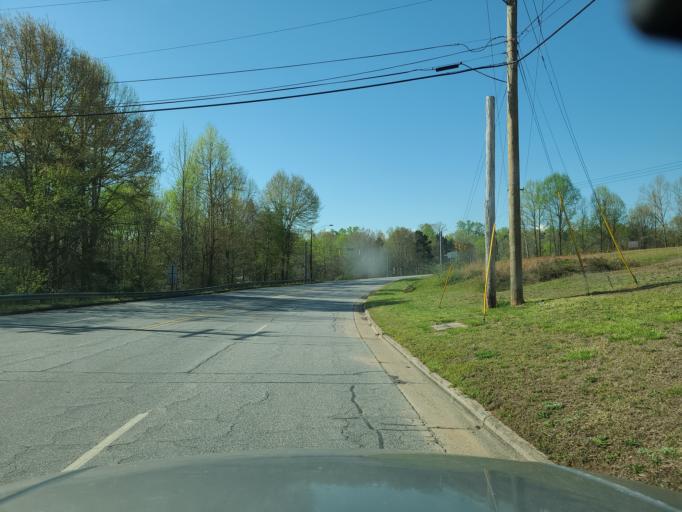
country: US
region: North Carolina
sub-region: Rutherford County
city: Spindale
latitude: 35.3496
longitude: -81.9365
